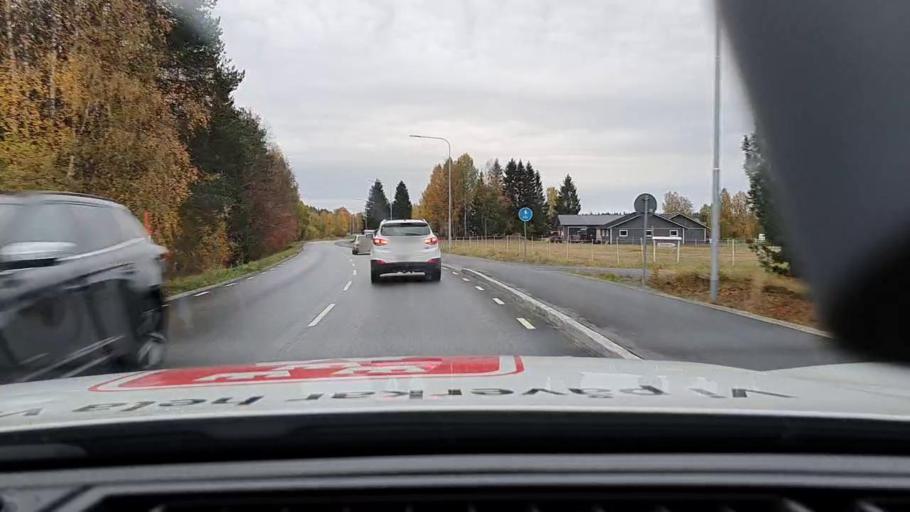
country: SE
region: Norrbotten
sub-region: Bodens Kommun
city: Saevast
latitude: 65.7735
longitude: 21.6974
